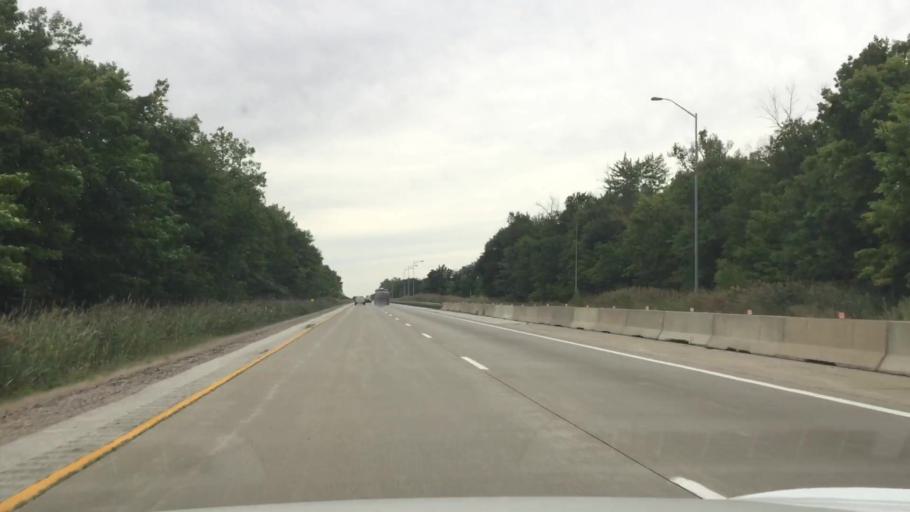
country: CA
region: Ontario
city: Camlachie
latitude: 42.9924
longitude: -82.1680
